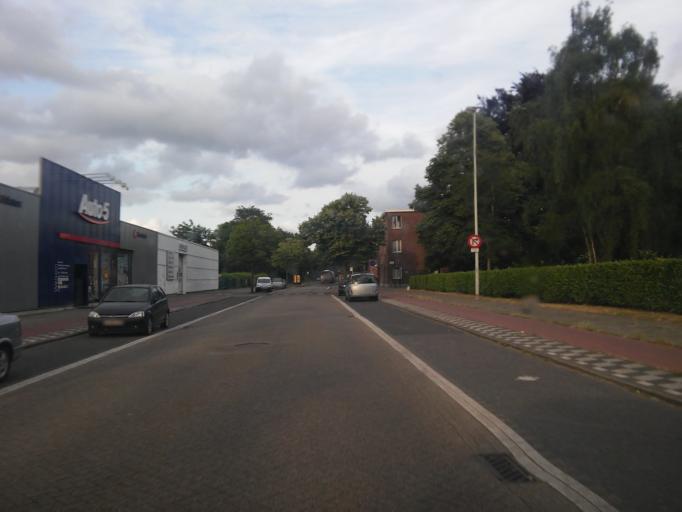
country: BE
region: Flanders
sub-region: Provincie Antwerpen
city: Aartselaar
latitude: 51.1728
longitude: 4.4015
